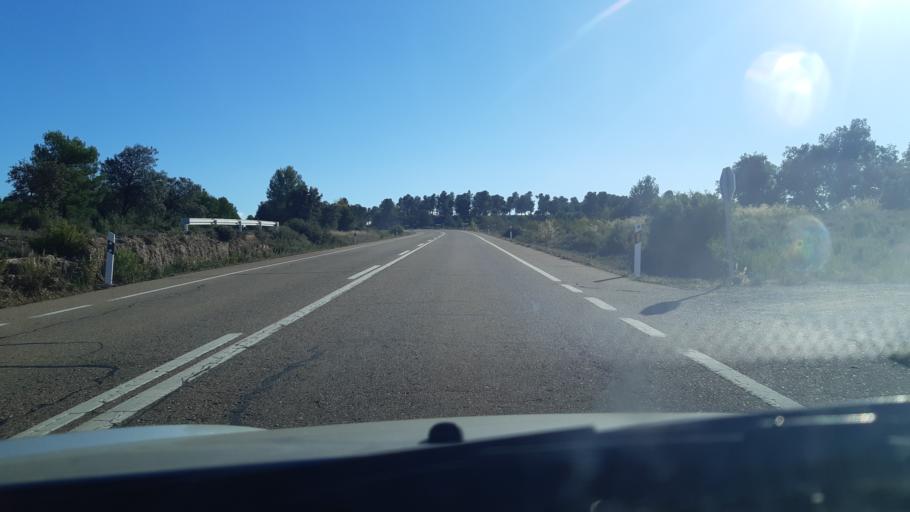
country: ES
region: Aragon
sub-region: Provincia de Teruel
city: Valjunquera
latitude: 40.9445
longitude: -0.0115
